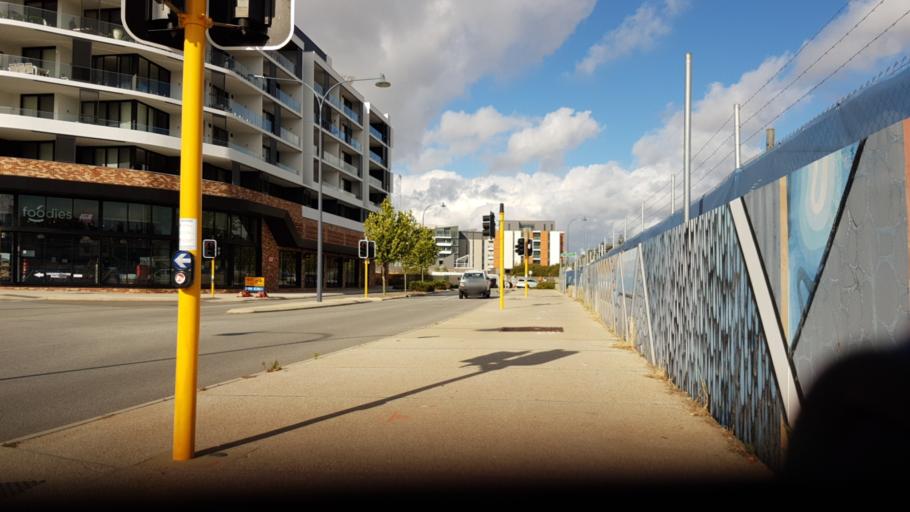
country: AU
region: Western Australia
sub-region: Claremont
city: Claremont
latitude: -31.9802
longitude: 115.7815
